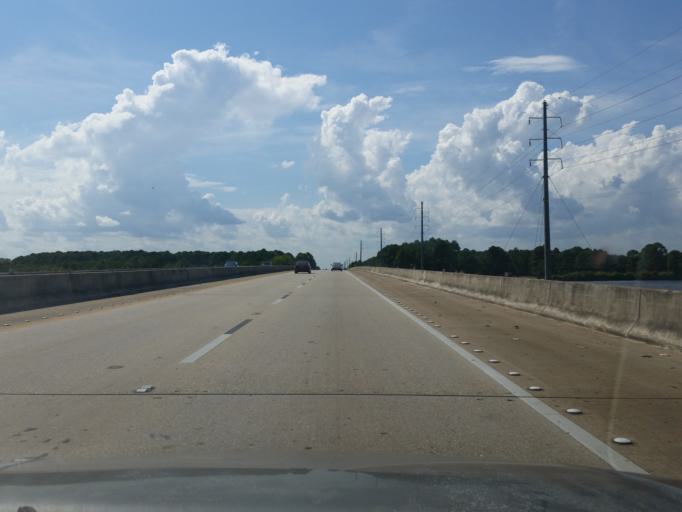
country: US
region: Alabama
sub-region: Baldwin County
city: Spanish Fort
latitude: 30.6679
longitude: -87.9239
